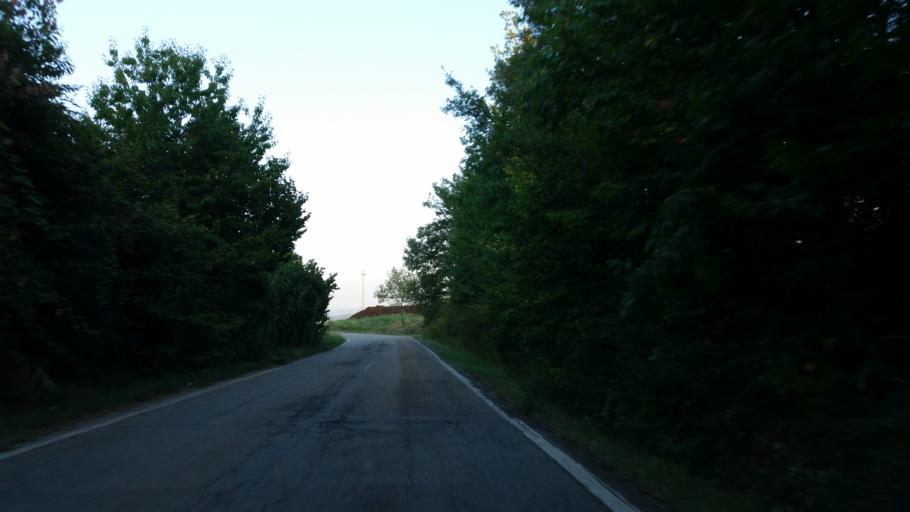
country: IT
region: Piedmont
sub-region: Provincia di Cuneo
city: Benevello
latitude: 44.6521
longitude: 8.1240
